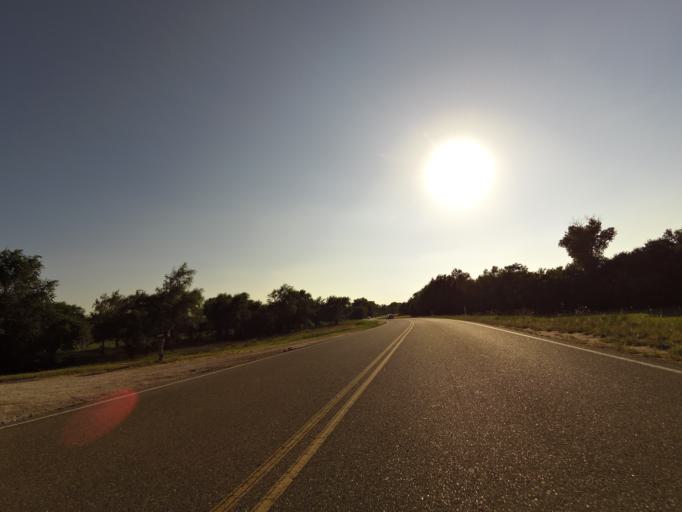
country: US
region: Kansas
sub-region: Reno County
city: Buhler
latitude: 38.1487
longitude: -97.8346
